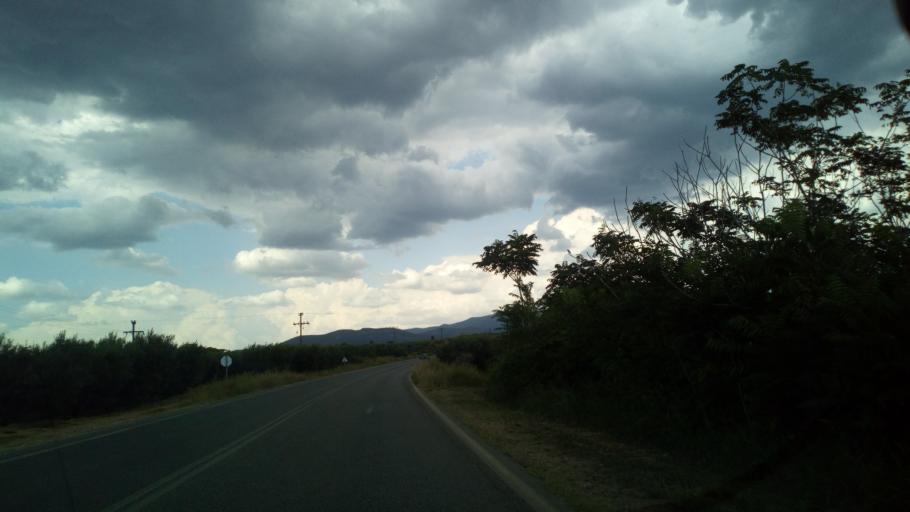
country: GR
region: Central Macedonia
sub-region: Nomos Chalkidikis
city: Kalyves Polygyrou
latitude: 40.2984
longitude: 23.4320
